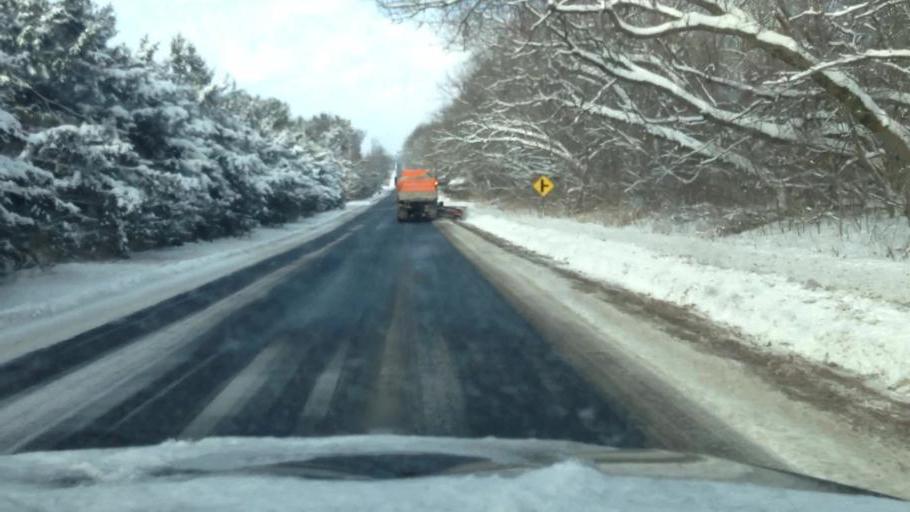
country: US
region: Wisconsin
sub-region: Walworth County
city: East Troy
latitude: 42.7608
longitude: -88.4456
